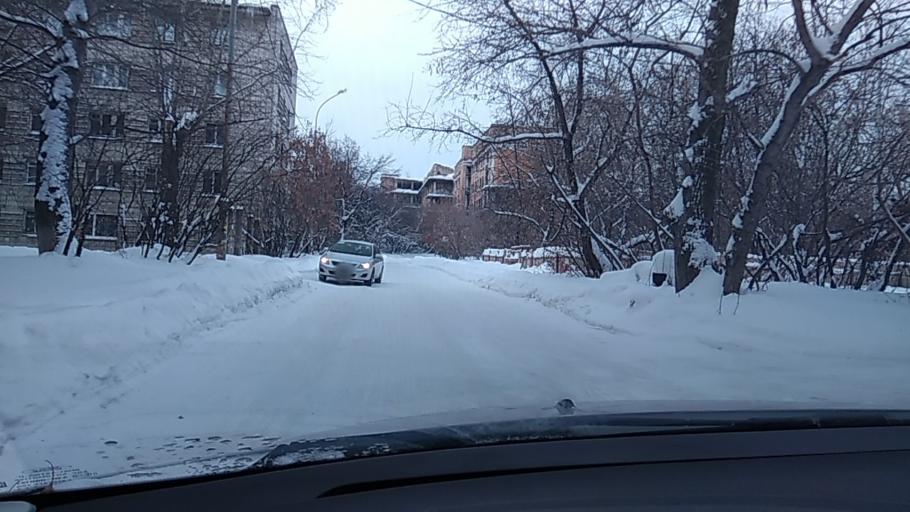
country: RU
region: Sverdlovsk
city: Yekaterinburg
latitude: 56.8195
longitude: 60.6046
